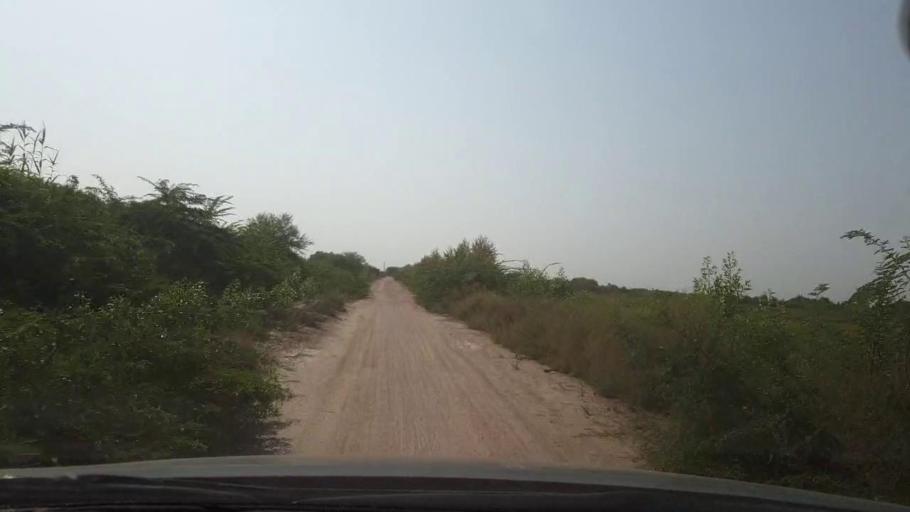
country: PK
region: Sindh
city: Naukot
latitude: 24.7843
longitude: 69.1952
